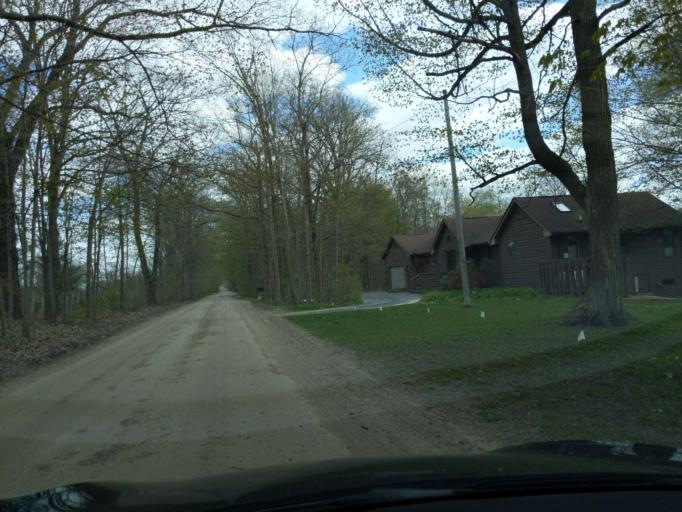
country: US
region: Michigan
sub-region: Eaton County
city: Dimondale
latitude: 42.6287
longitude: -84.6114
